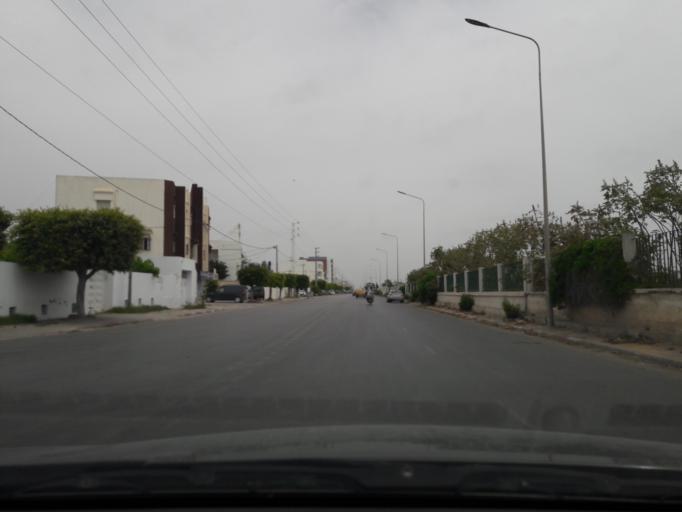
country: TN
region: Safaqis
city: Al Qarmadah
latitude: 34.7940
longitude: 10.7604
